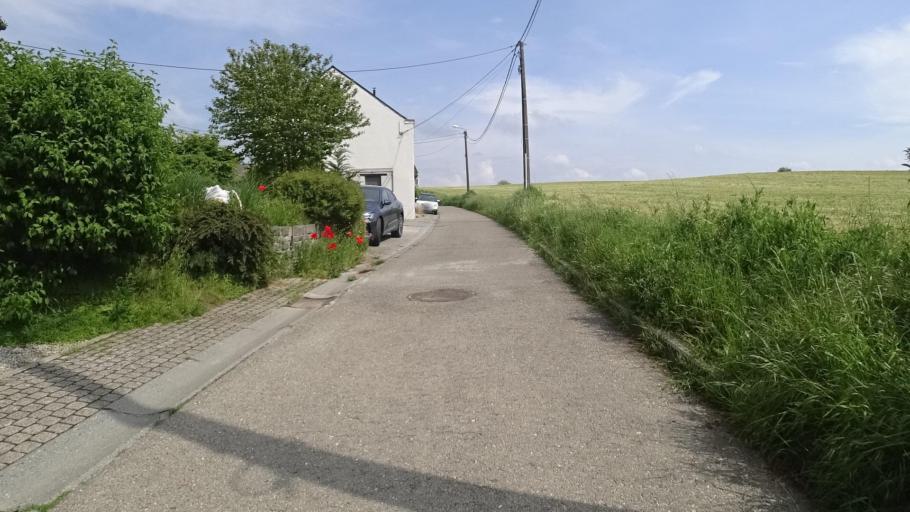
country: BE
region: Wallonia
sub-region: Province du Brabant Wallon
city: Louvain-la-Neuve
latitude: 50.6748
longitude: 4.6398
